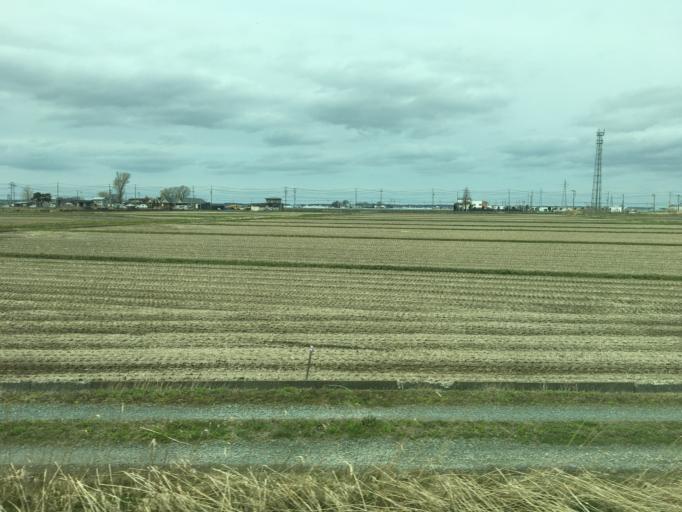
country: JP
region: Aomori
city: Shimokizukuri
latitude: 40.7993
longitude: 140.3813
